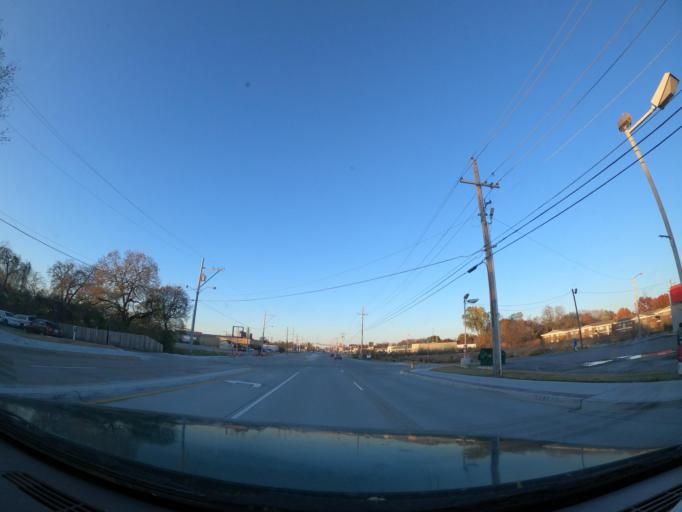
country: US
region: Oklahoma
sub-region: Tulsa County
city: Tulsa
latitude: 36.1386
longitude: -95.8866
